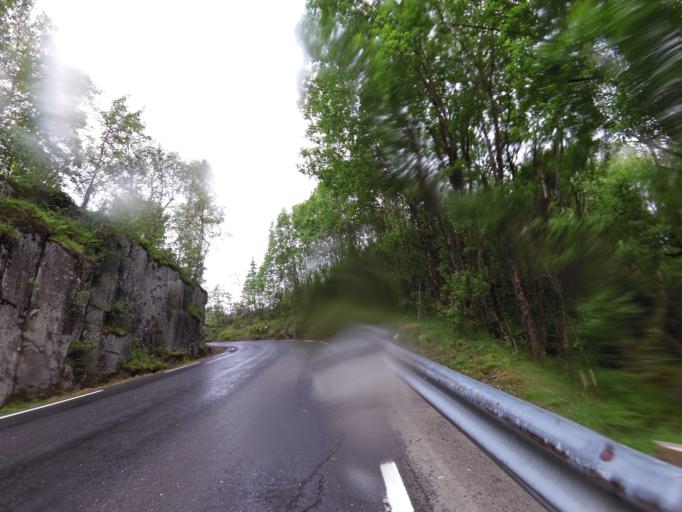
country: NO
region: Vest-Agder
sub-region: Lyngdal
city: Lyngdal
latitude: 58.1124
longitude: 7.0837
